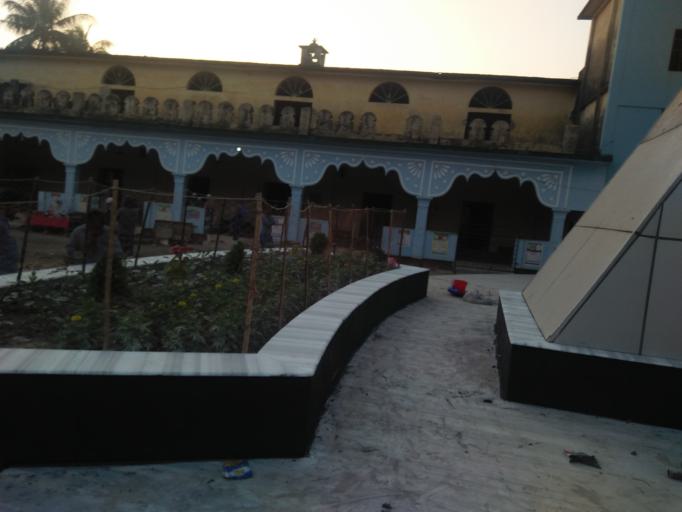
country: BD
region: Khulna
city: Uttar Char Fasson
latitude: 22.1861
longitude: 90.7591
